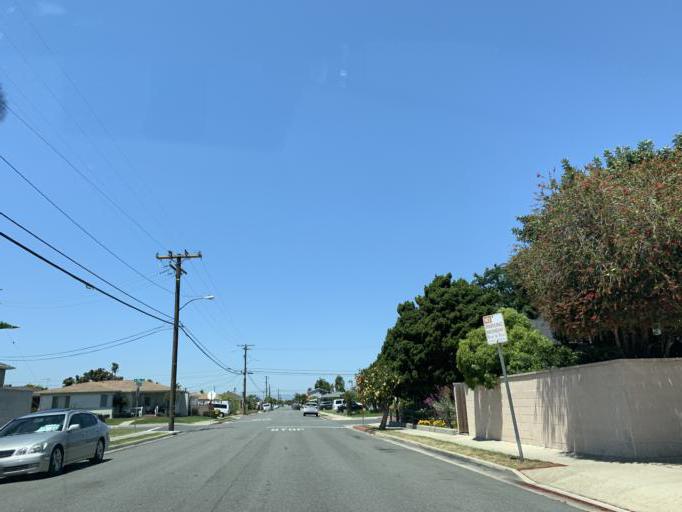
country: US
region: California
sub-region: Los Angeles County
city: Gardena
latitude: 33.8916
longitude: -118.3114
